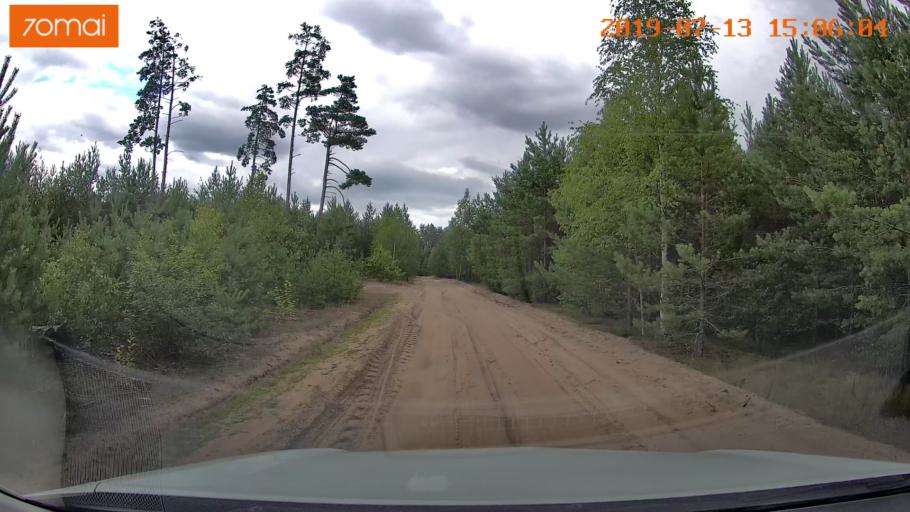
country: BY
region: Mogilev
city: Asipovichy
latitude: 53.2009
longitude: 28.7535
